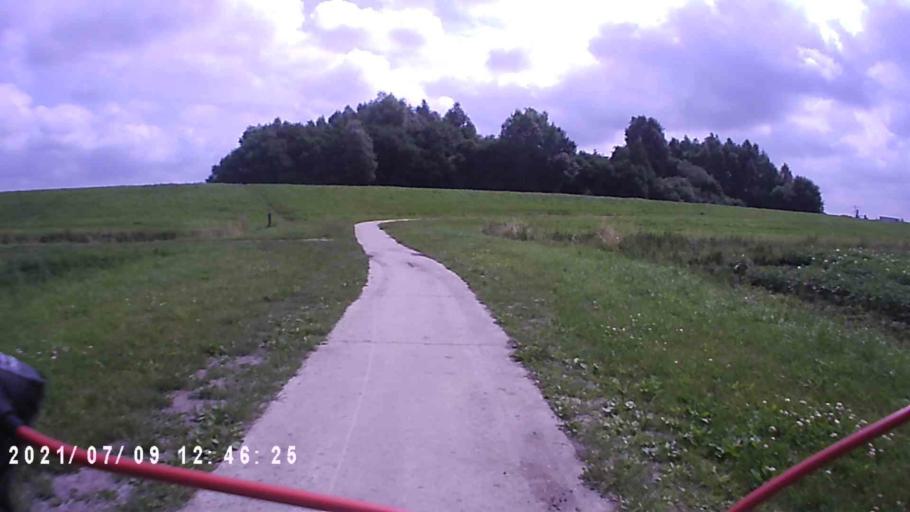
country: NL
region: Groningen
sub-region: Gemeente  Oldambt
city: Winschoten
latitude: 53.1289
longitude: 7.0286
